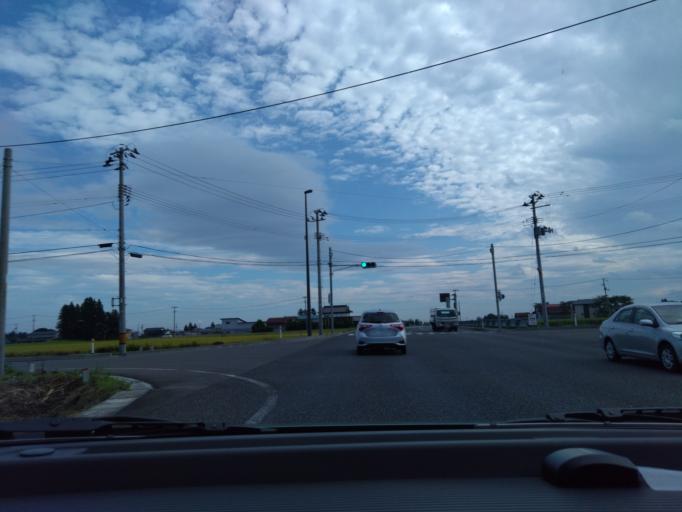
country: JP
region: Iwate
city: Hanamaki
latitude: 39.3740
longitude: 141.0571
